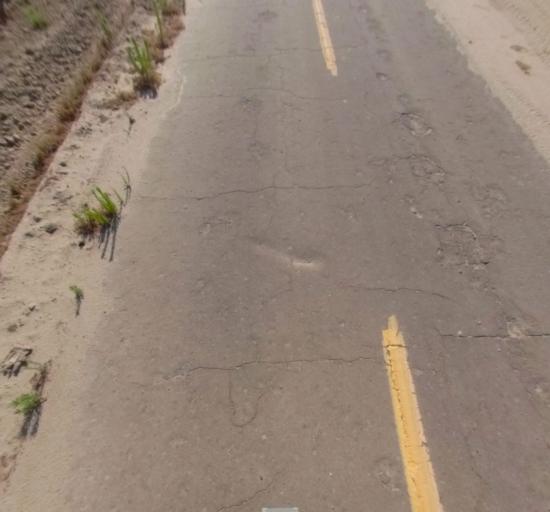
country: US
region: California
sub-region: Fresno County
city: Biola
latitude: 36.8440
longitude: -120.1123
